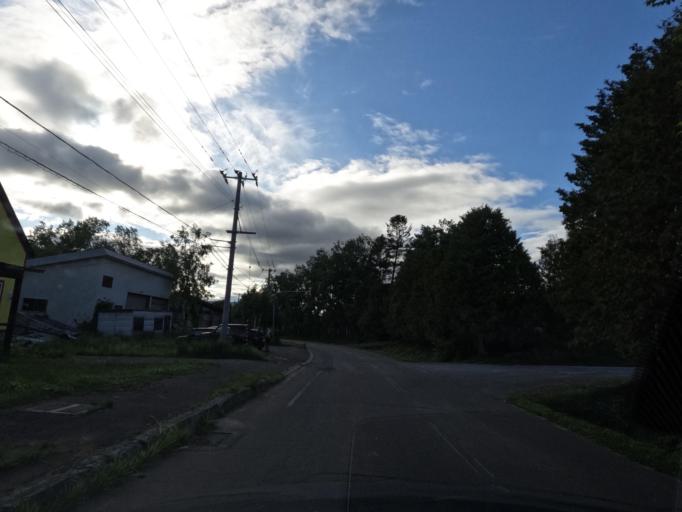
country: JP
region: Hokkaido
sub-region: Asahikawa-shi
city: Asahikawa
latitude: 43.6297
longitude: 142.4394
